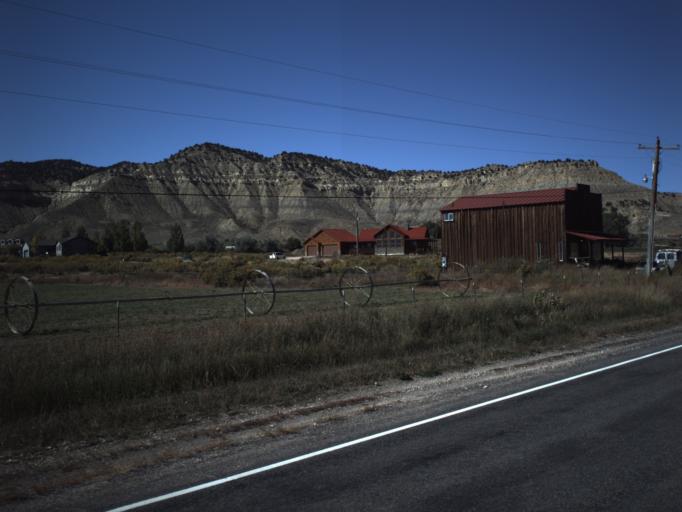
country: US
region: Utah
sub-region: Garfield County
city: Panguitch
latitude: 37.6310
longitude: -112.0818
